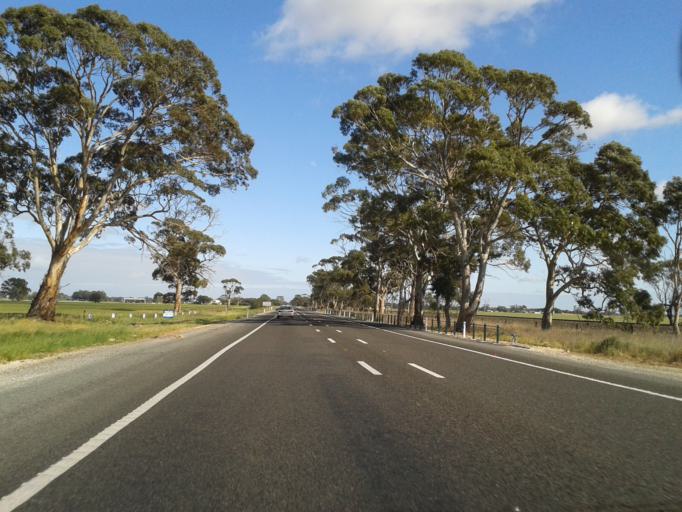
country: AU
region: South Australia
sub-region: Tatiara
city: Bordertown
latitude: -36.2759
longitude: 140.7176
